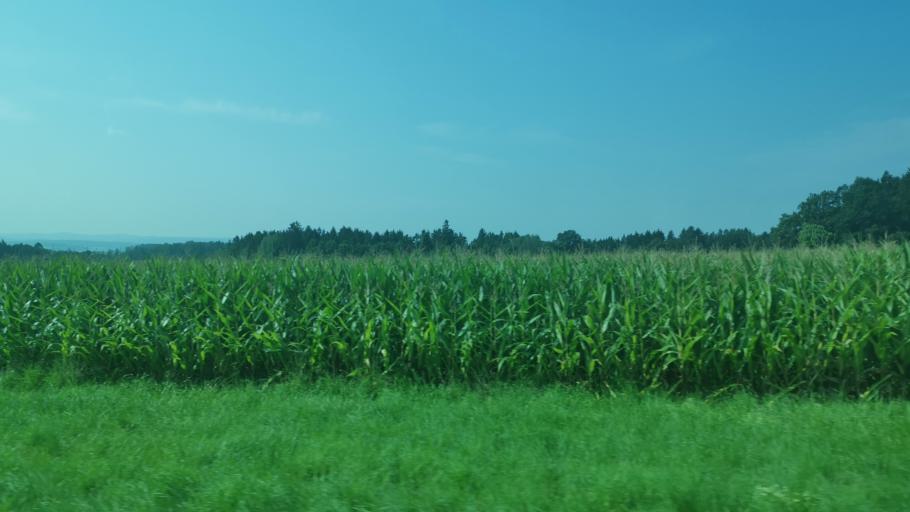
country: DE
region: Bavaria
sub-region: Upper Palatinate
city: Pemfling
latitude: 49.2614
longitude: 12.6346
